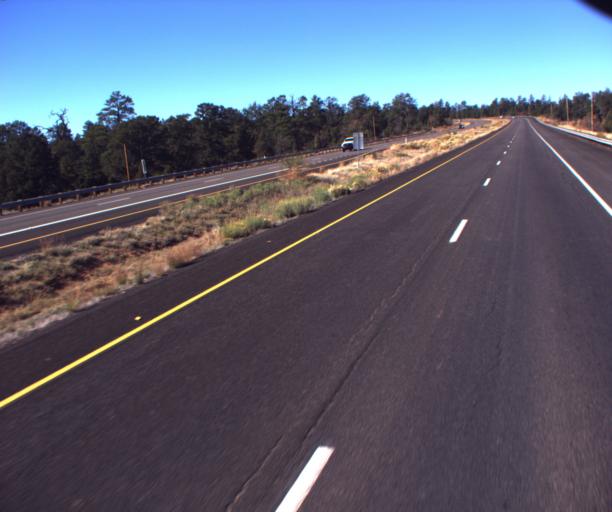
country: US
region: Arizona
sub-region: Apache County
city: Saint Michaels
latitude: 35.6661
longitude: -109.1625
